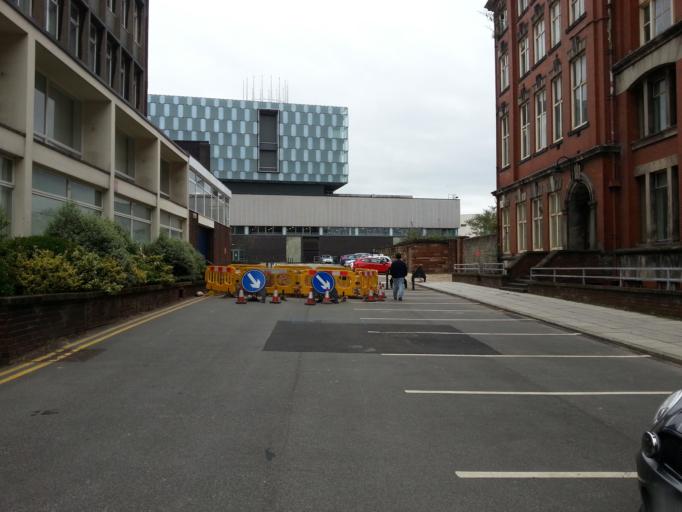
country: GB
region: England
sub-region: Liverpool
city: Liverpool
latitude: 53.4070
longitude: -2.9687
